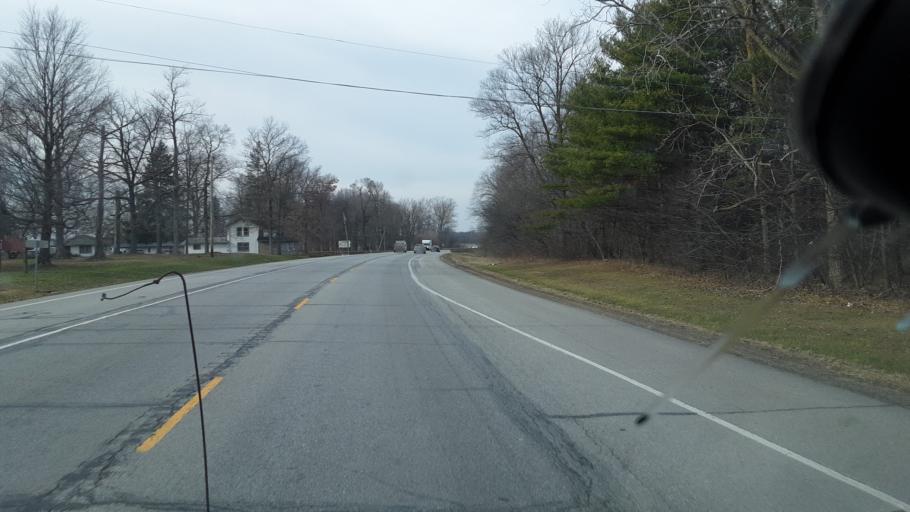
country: US
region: Indiana
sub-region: DeKalb County
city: Waterloo
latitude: 41.4351
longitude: -85.0310
